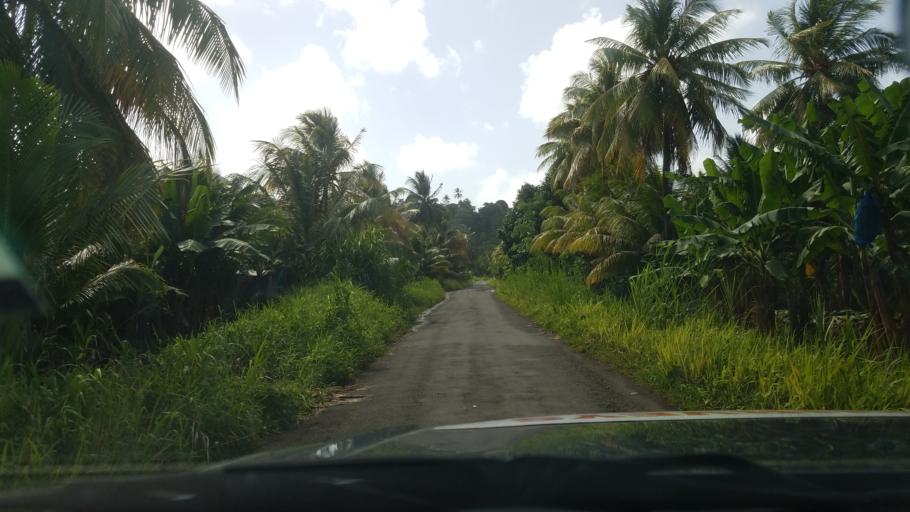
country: LC
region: Anse-la-Raye
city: Anse La Raye
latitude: 13.9547
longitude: -61.0050
